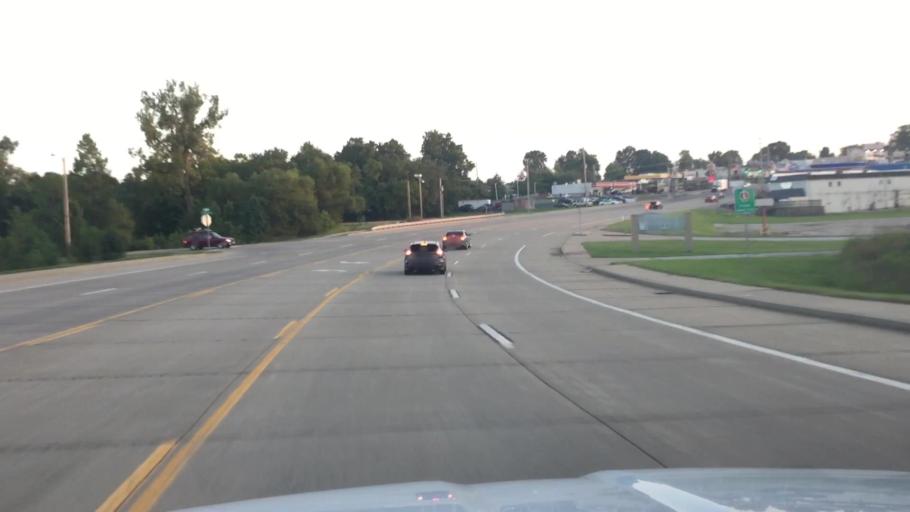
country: US
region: Missouri
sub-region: Jefferson County
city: Arnold
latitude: 38.4551
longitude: -90.3607
